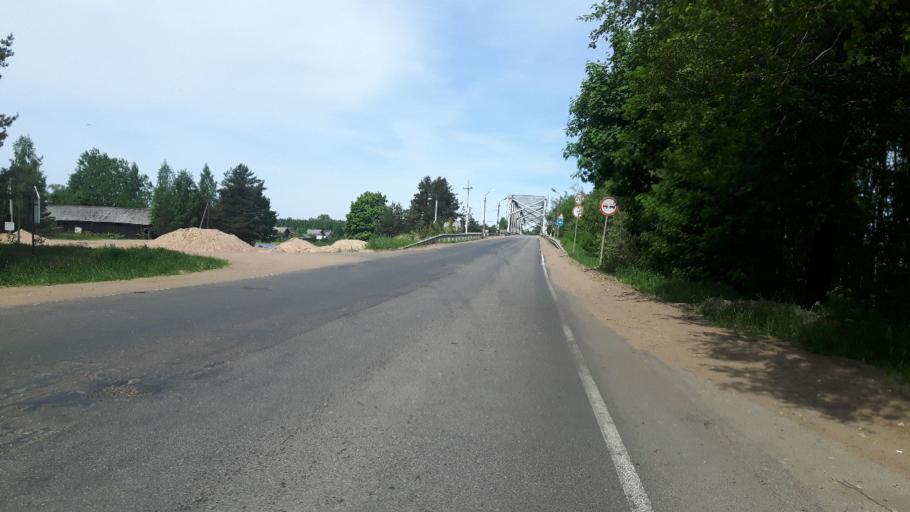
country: RU
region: Leningrad
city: Ust'-Luga
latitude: 59.6508
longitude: 28.2604
